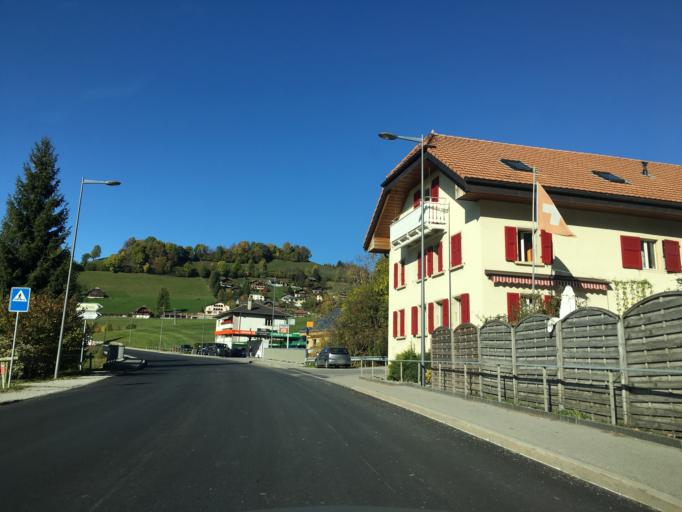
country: CH
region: Fribourg
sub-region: Gruyere District
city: Charmey
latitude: 46.6154
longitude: 7.1700
